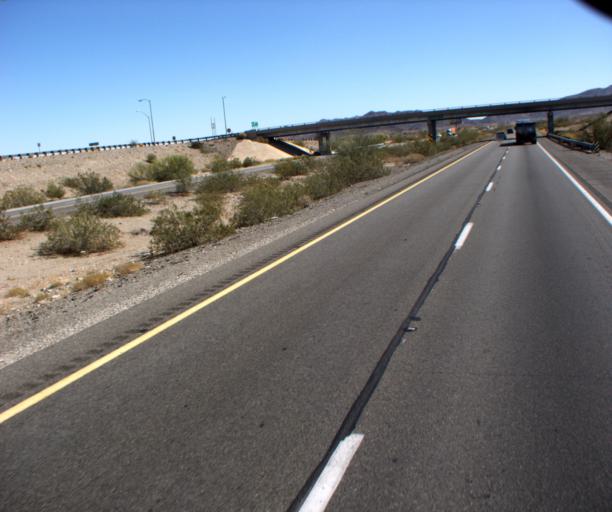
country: US
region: Arizona
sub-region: La Paz County
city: Ehrenberg
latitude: 33.6238
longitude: -114.4352
